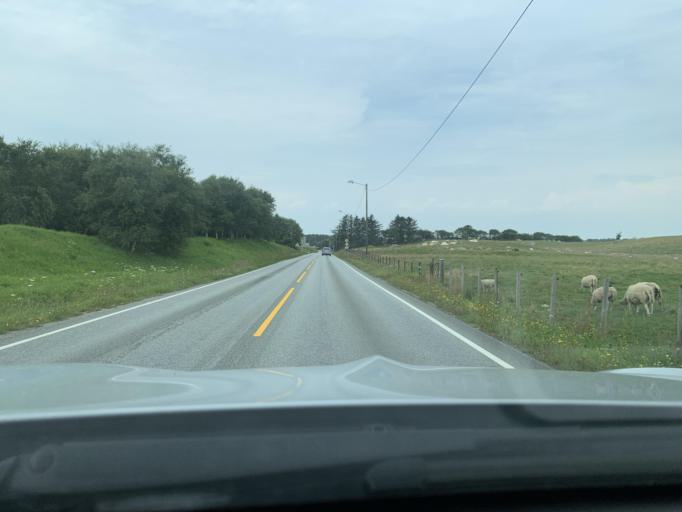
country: NO
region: Rogaland
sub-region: Time
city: Bryne
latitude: 58.7331
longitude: 5.6783
